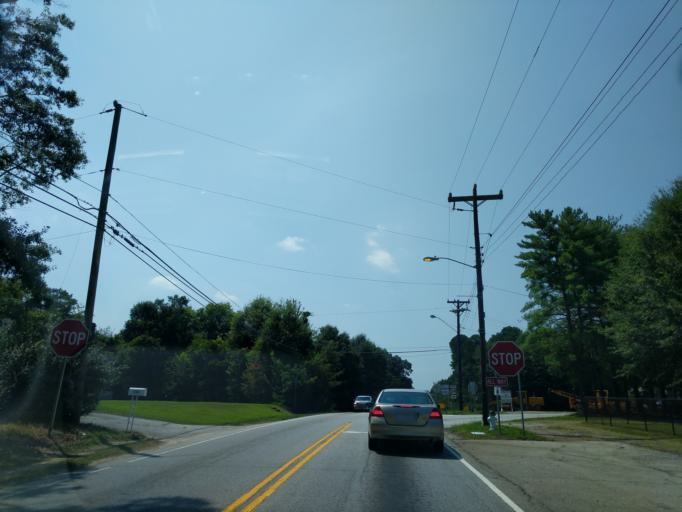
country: US
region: South Carolina
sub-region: Spartanburg County
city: Duncan
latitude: 34.9391
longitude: -82.1494
